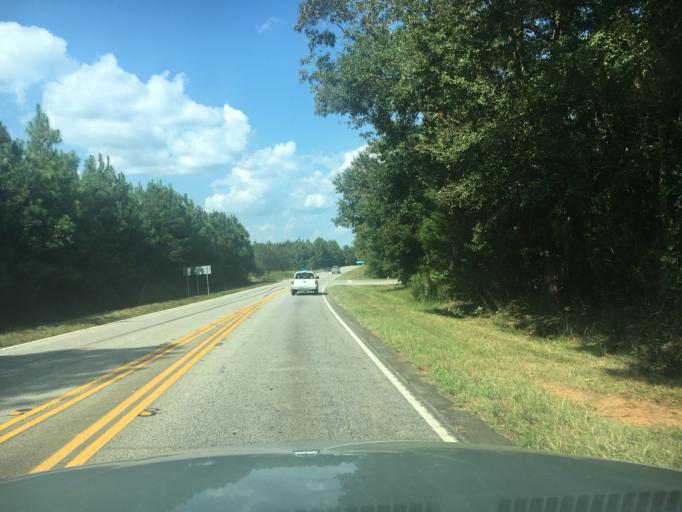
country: US
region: South Carolina
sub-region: Anderson County
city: Pendleton
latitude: 34.6164
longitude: -82.7835
